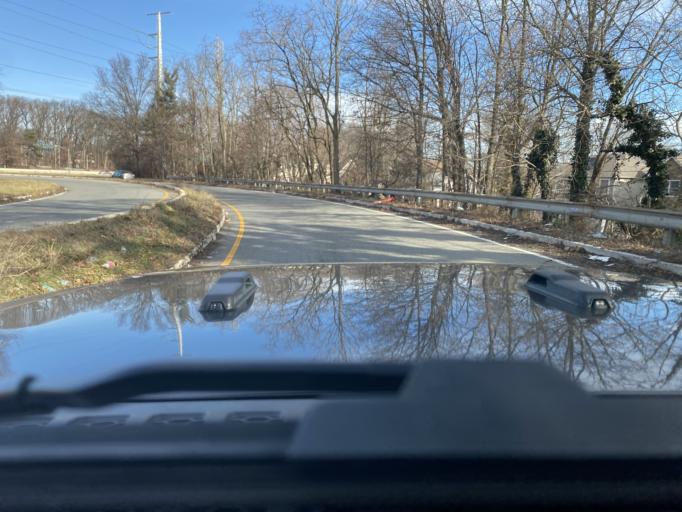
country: US
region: New Jersey
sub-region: Middlesex County
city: Metuchen
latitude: 40.5244
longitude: -74.3573
